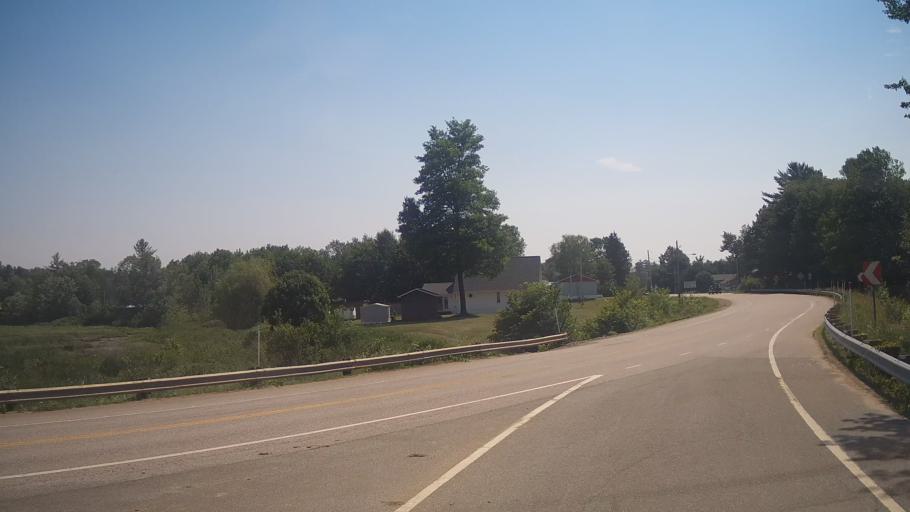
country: CA
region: Quebec
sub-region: Outaouais
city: Fort-Coulonge
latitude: 45.9113
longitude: -76.9205
